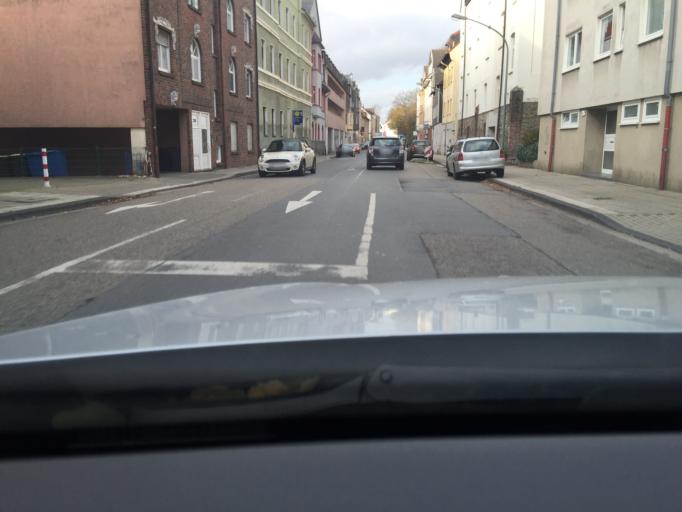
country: DE
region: North Rhine-Westphalia
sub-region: Regierungsbezirk Dusseldorf
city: Velbert
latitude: 51.3861
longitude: 7.0857
